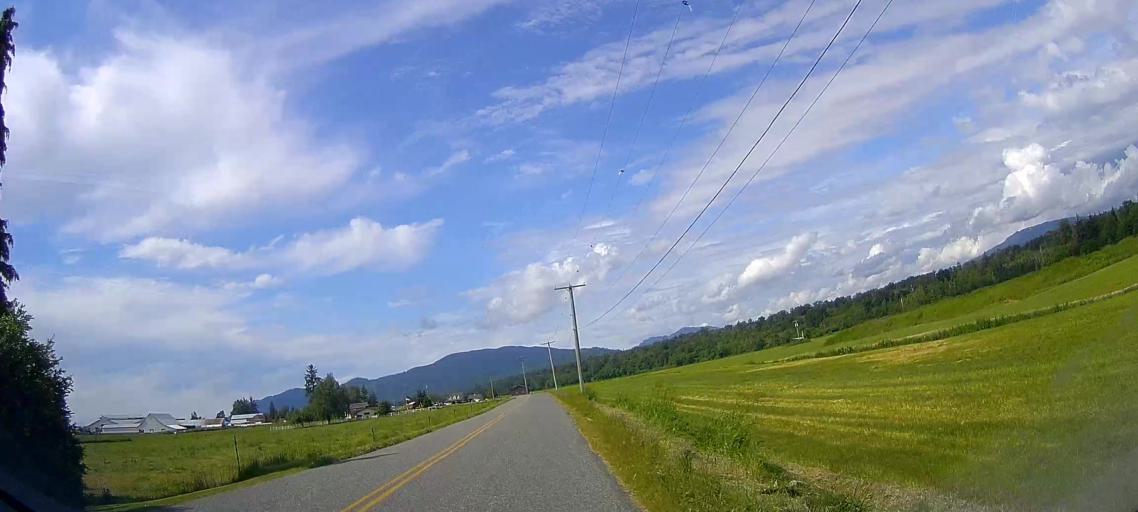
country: US
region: Washington
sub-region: Skagit County
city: Burlington
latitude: 48.5375
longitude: -122.3880
